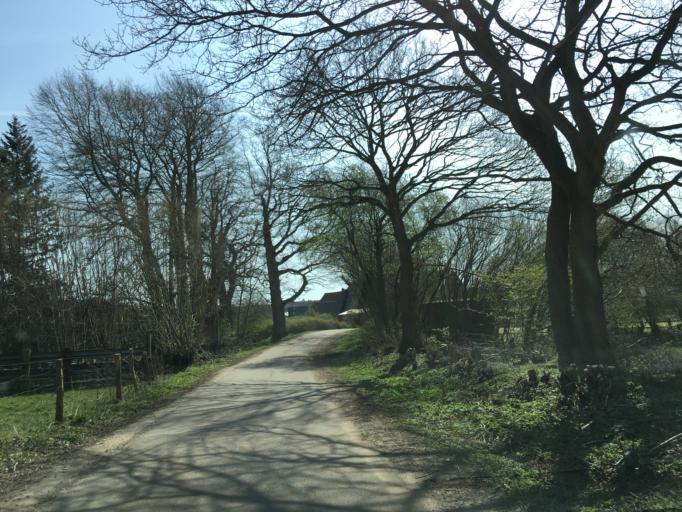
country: DE
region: Schleswig-Holstein
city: Felm
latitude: 54.4142
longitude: 10.0776
